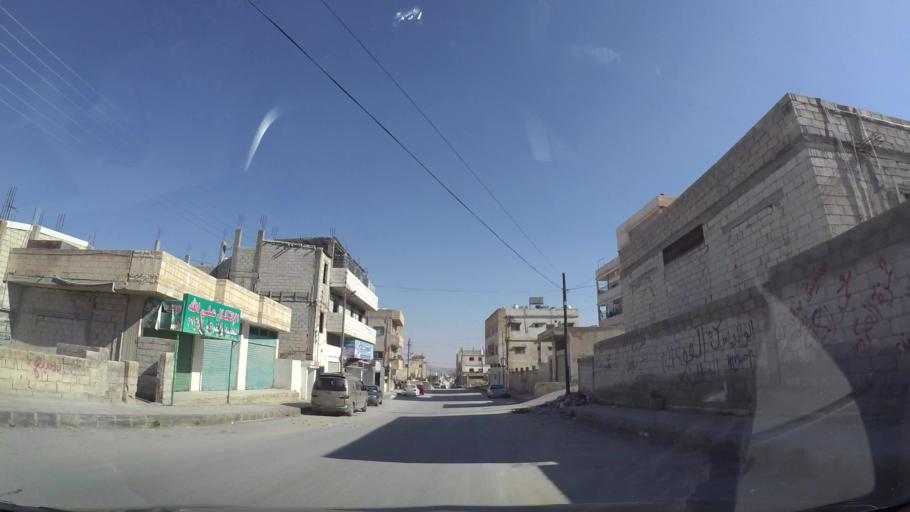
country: JO
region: Zarqa
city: Russeifa
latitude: 32.0357
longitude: 36.0347
